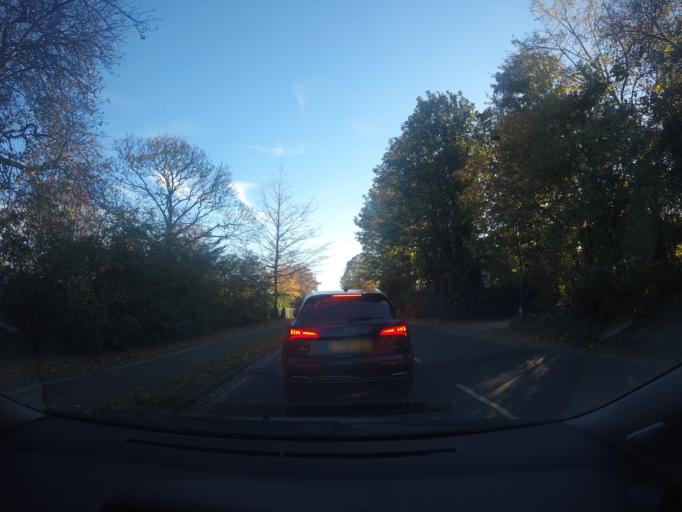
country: GB
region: England
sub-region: City of York
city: York
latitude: 53.9758
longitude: -1.0821
